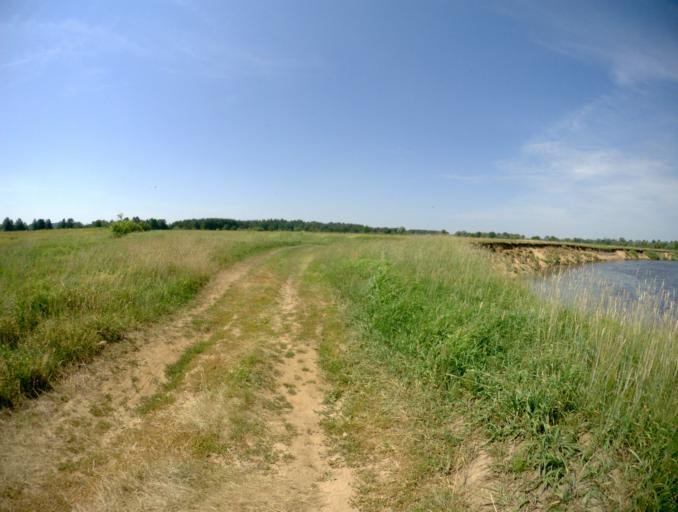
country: RU
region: Vladimir
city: Vorsha
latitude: 56.0350
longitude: 40.1817
